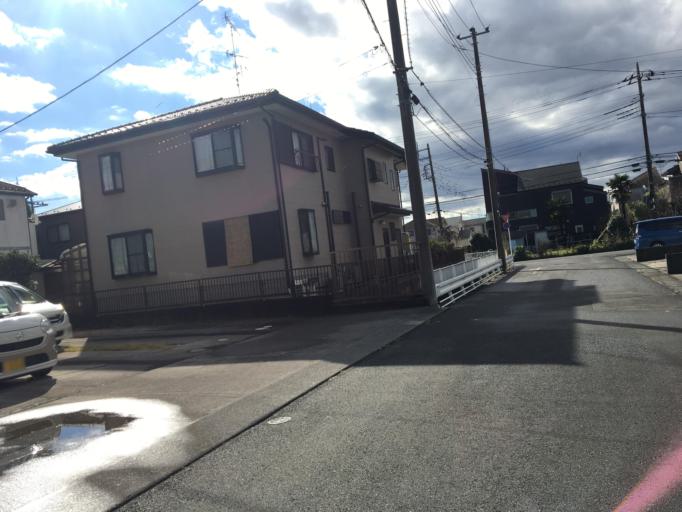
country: JP
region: Saitama
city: Koshigaya
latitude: 35.9248
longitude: 139.8098
